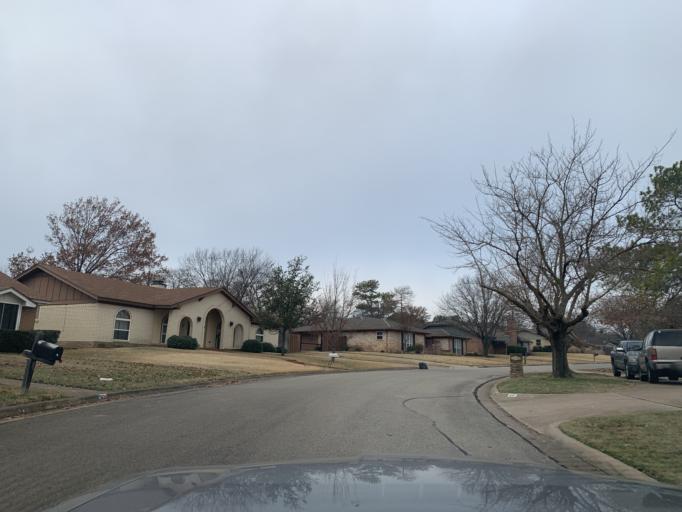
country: US
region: Texas
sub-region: Tarrant County
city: Bedford
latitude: 32.8350
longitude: -97.1523
